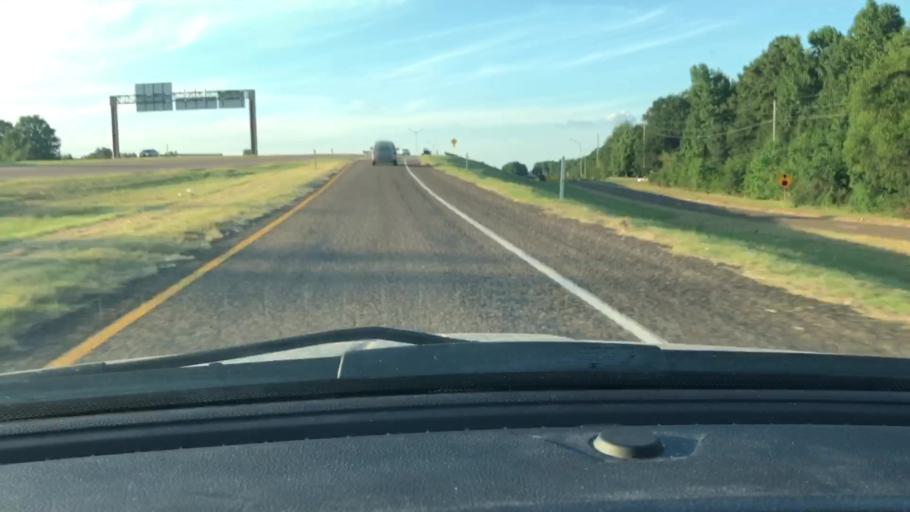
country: US
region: Texas
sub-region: Bowie County
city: Wake Village
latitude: 33.3998
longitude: -94.0971
